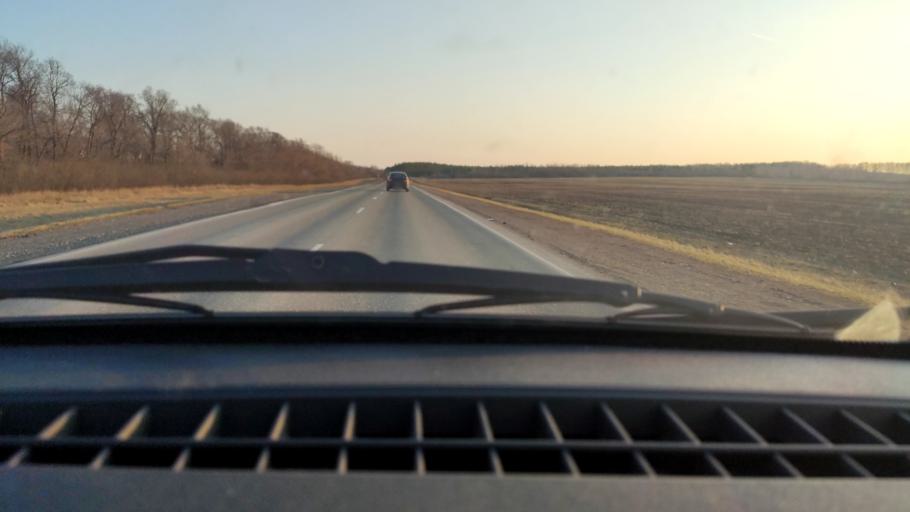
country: RU
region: Bashkortostan
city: Davlekanovo
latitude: 54.2526
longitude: 55.0825
